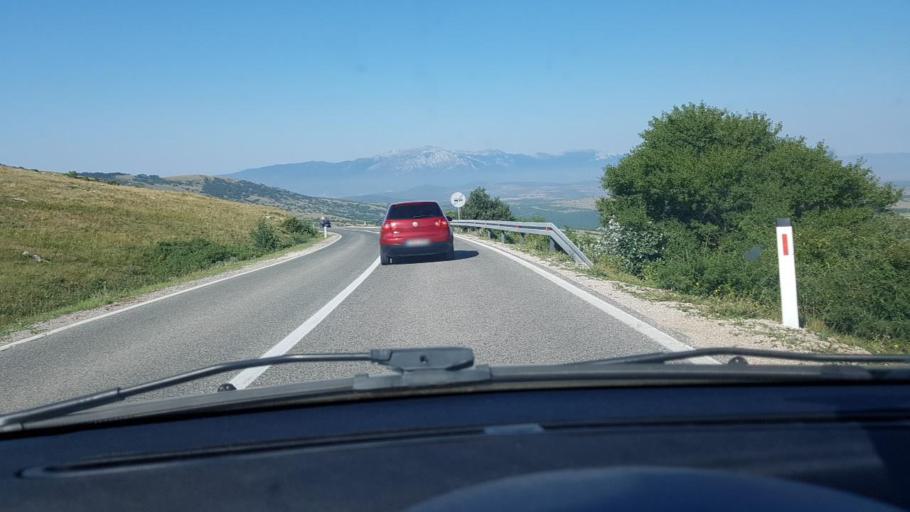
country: BA
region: Federation of Bosnia and Herzegovina
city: Vidosi
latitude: 43.7829
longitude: 17.1266
